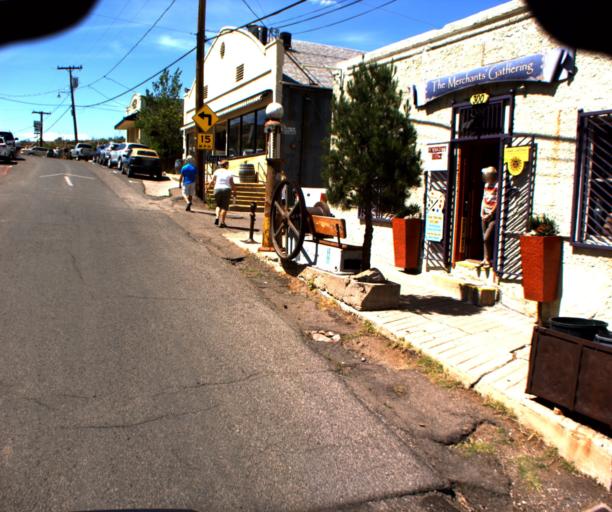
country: US
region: Arizona
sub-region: Yavapai County
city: Clarkdale
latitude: 34.7509
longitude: -112.1153
